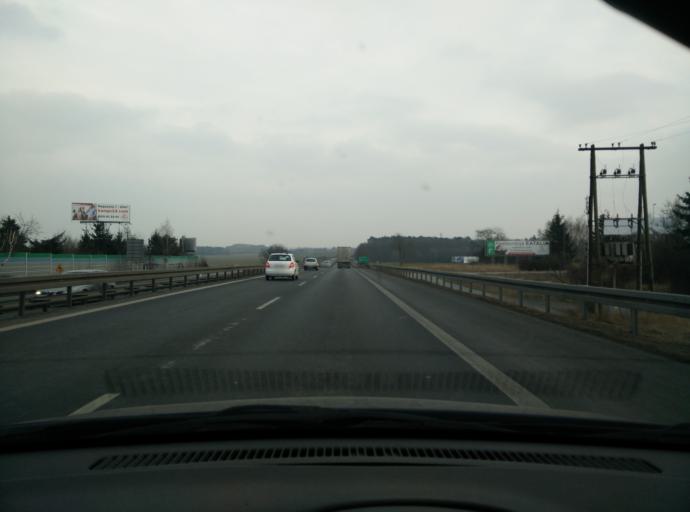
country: PL
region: Greater Poland Voivodeship
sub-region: Powiat poznanski
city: Daszewice
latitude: 52.3314
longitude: 17.0219
